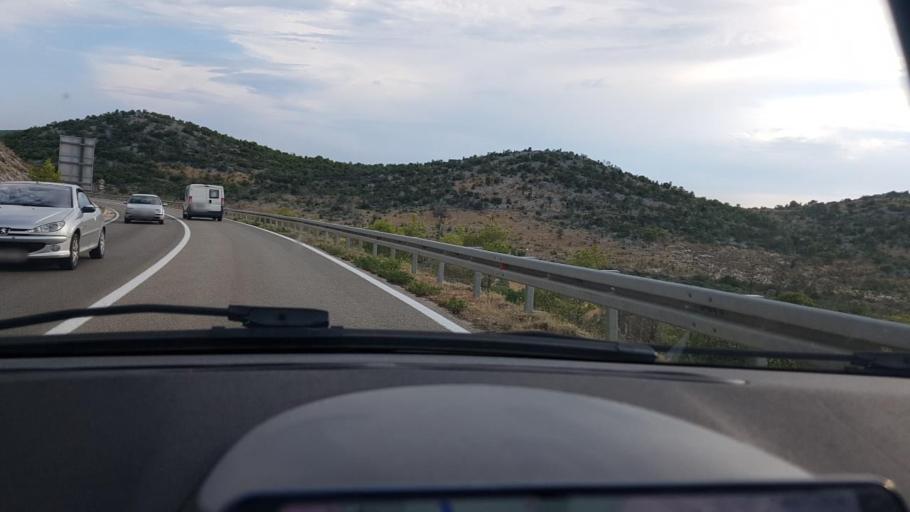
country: HR
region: Sibensko-Kniniska
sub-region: Grad Sibenik
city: Sibenik
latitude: 43.7541
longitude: 15.9364
